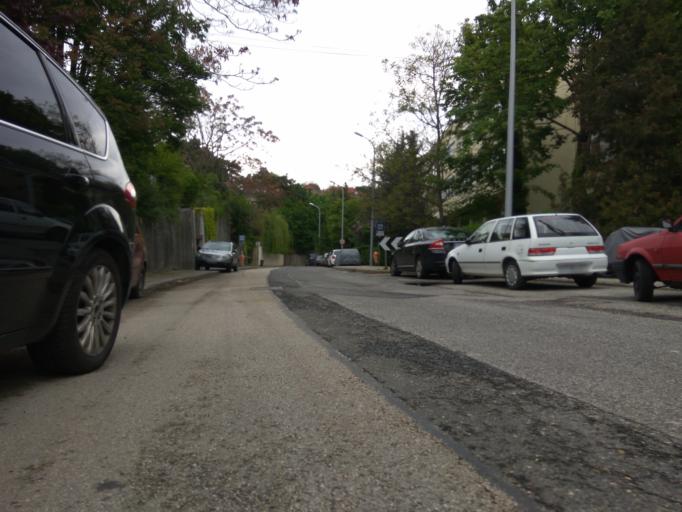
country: HU
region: Budapest
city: Budapest XII. keruelet
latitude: 47.4966
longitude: 18.9980
